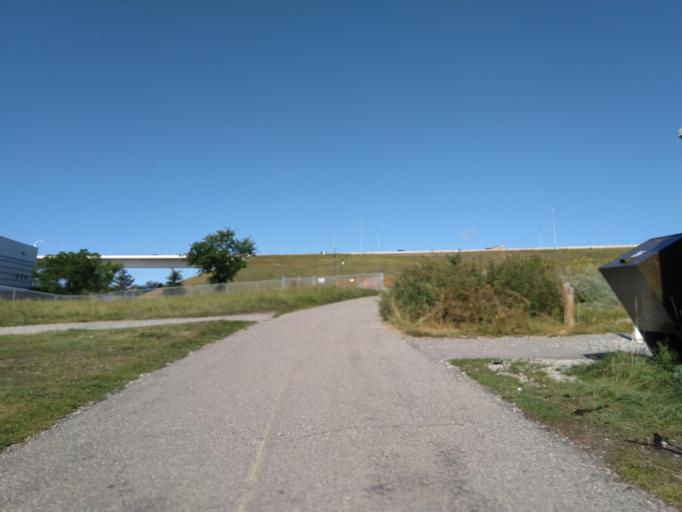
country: CA
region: Alberta
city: Calgary
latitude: 51.1001
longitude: -114.2271
